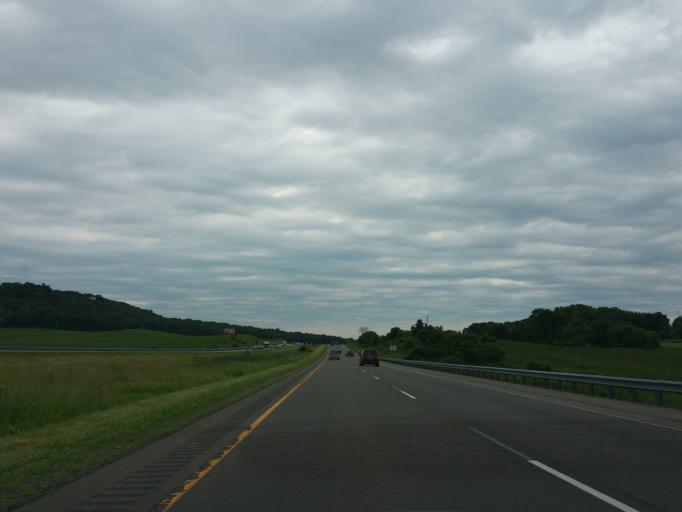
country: US
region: Wisconsin
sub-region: Jackson County
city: Black River Falls
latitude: 44.4057
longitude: -91.0282
